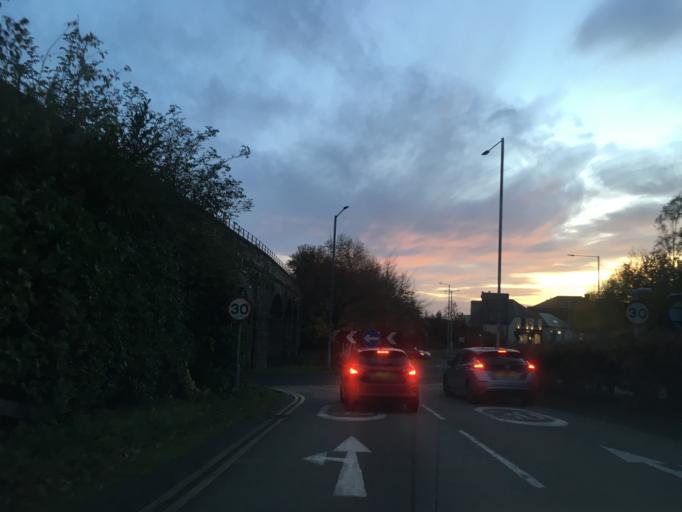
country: GB
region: Scotland
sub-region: Fife
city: Dunfermline
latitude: 56.0672
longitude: -3.4548
